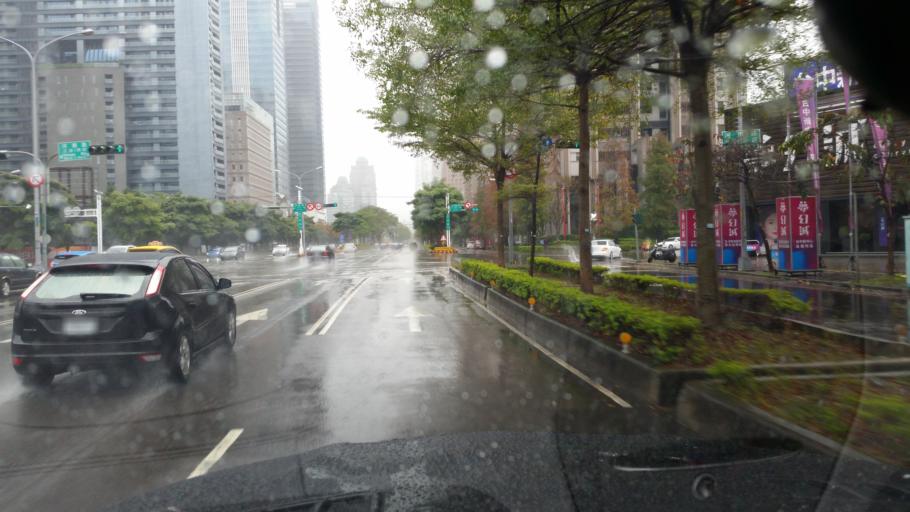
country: TW
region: Taiwan
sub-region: Taichung City
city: Taichung
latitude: 24.1606
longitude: 120.6358
